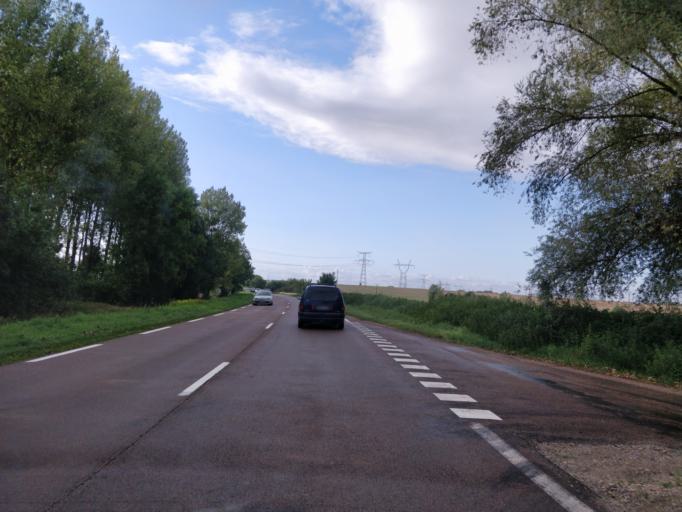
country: FR
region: Champagne-Ardenne
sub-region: Departement de l'Aube
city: Lusigny-sur-Barse
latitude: 48.2668
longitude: 4.2162
